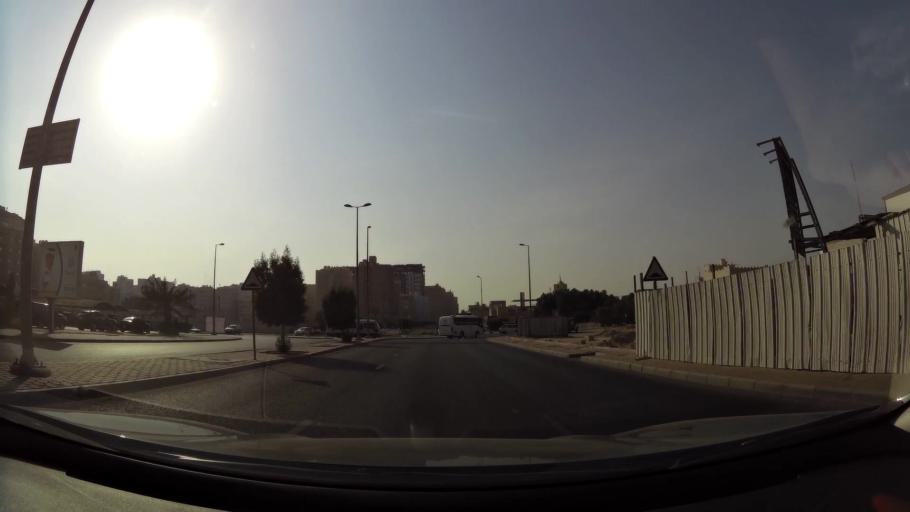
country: KW
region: Al Ahmadi
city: Al Fintas
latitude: 29.1706
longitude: 48.1199
